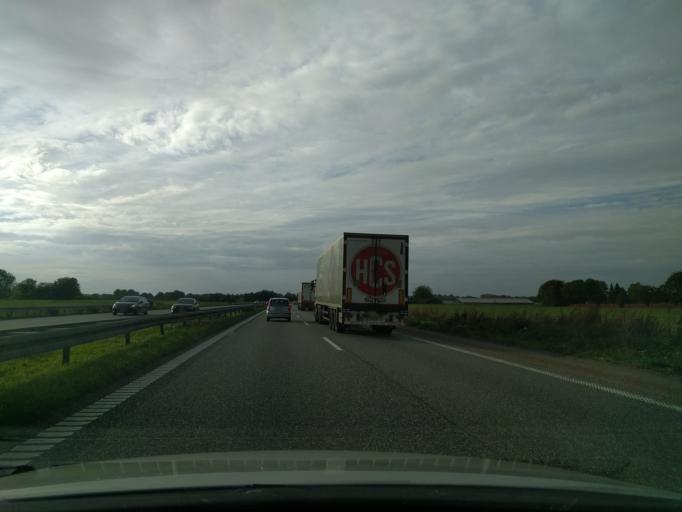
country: DK
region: Zealand
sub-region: Soro Kommune
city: Frederiksberg
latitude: 55.4490
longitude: 11.6361
